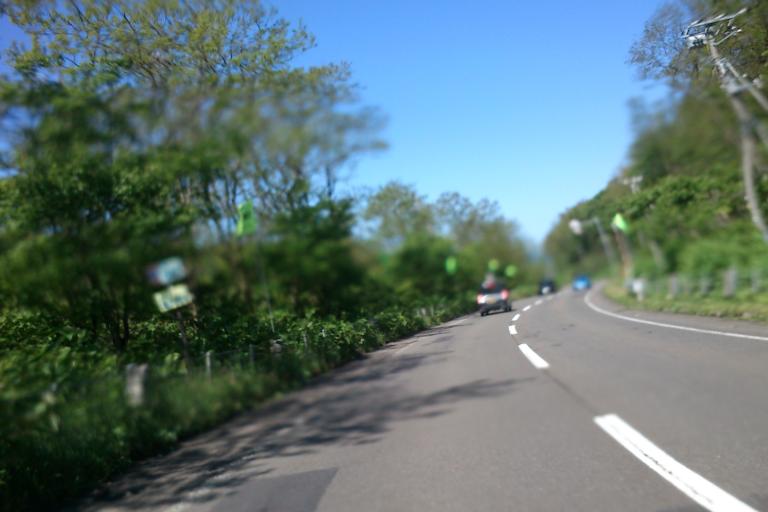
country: JP
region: Hokkaido
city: Ishikari
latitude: 43.5560
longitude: 141.4023
